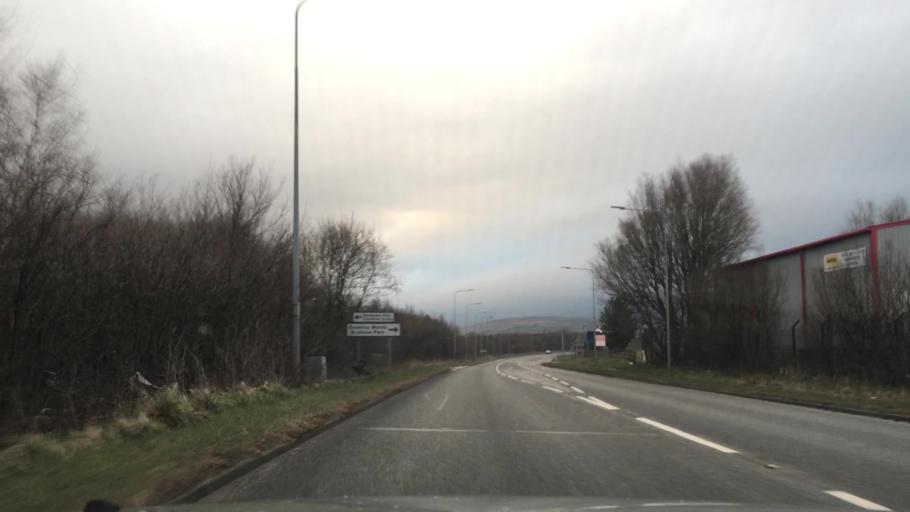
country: GB
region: England
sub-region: Cumbria
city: Askam in Furness
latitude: 54.1507
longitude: -3.2276
